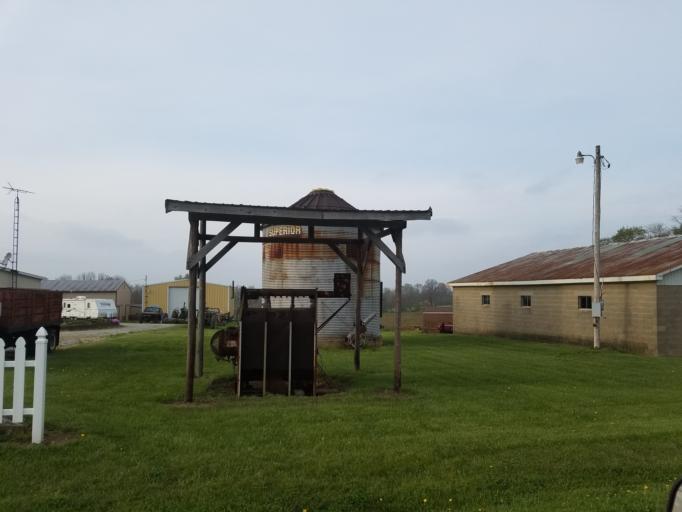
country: US
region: Ohio
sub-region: Knox County
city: Fredericktown
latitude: 40.4964
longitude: -82.6269
